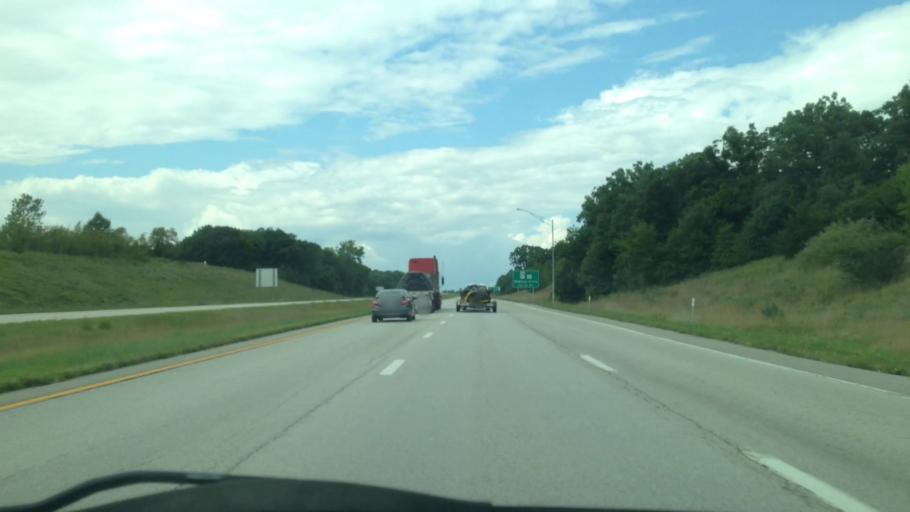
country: US
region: Missouri
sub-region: Pike County
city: Bowling Green
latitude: 39.3633
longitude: -91.2073
